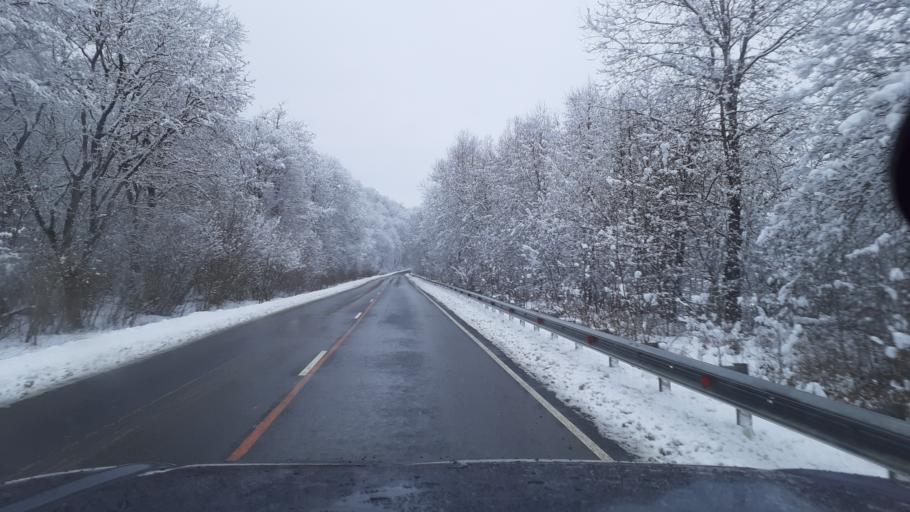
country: RU
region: Adygeya
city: Kamennomostskiy
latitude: 44.2073
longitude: 40.1801
